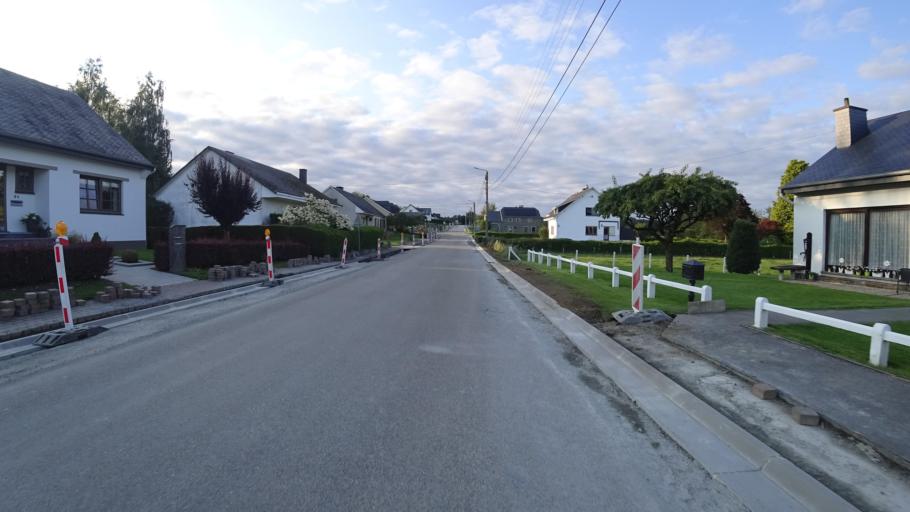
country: BE
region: Wallonia
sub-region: Province du Luxembourg
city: Neufchateau
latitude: 49.9054
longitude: 5.3875
